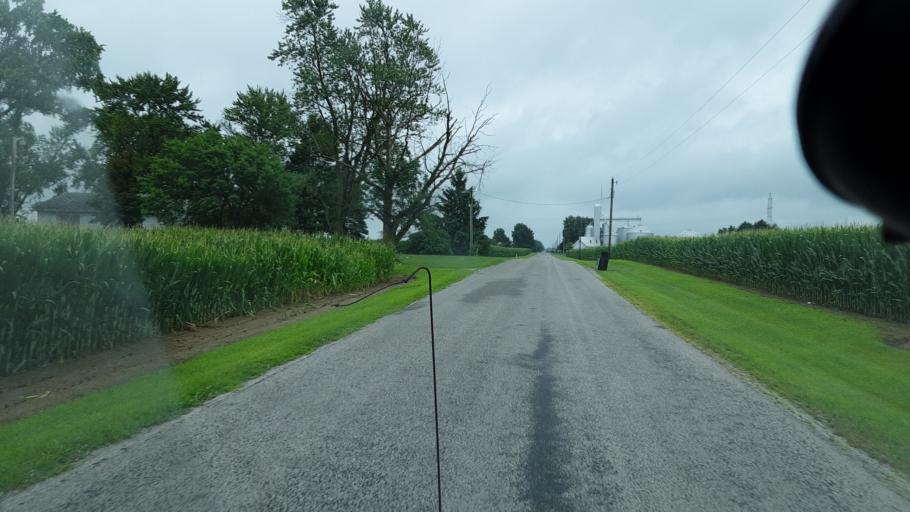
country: US
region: Indiana
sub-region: Wells County
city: Ossian
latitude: 40.9251
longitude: -85.1098
